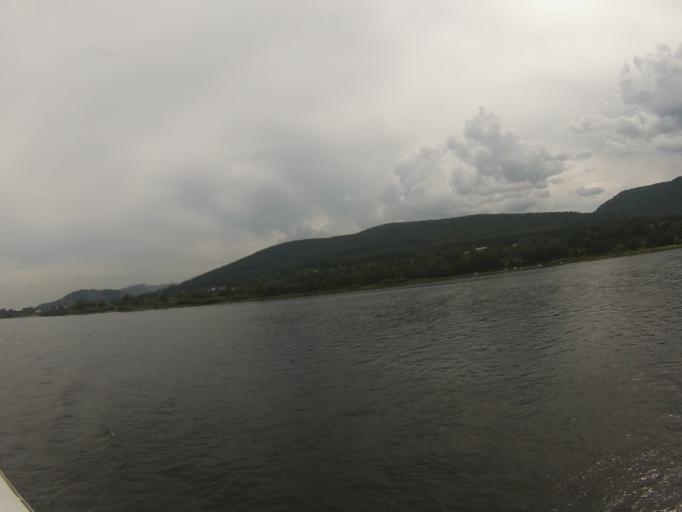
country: RU
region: Krasnoyarskiy
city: Krasnoyarsk
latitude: 55.9756
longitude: 92.7463
